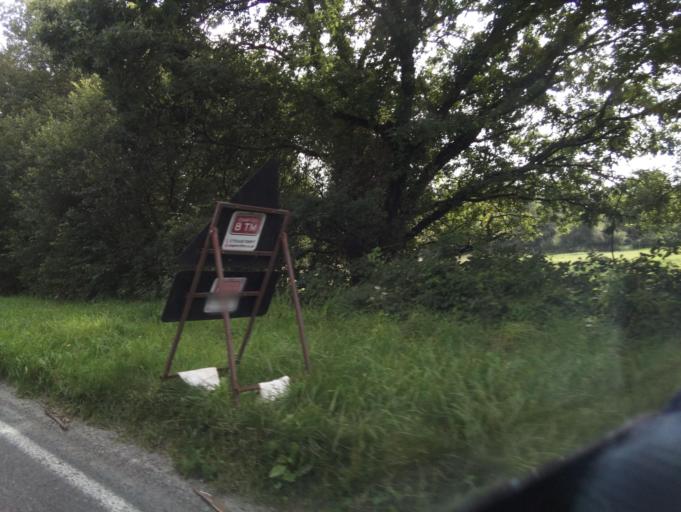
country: GB
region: England
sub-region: Hampshire
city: Marchwood
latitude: 50.8717
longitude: -1.4392
